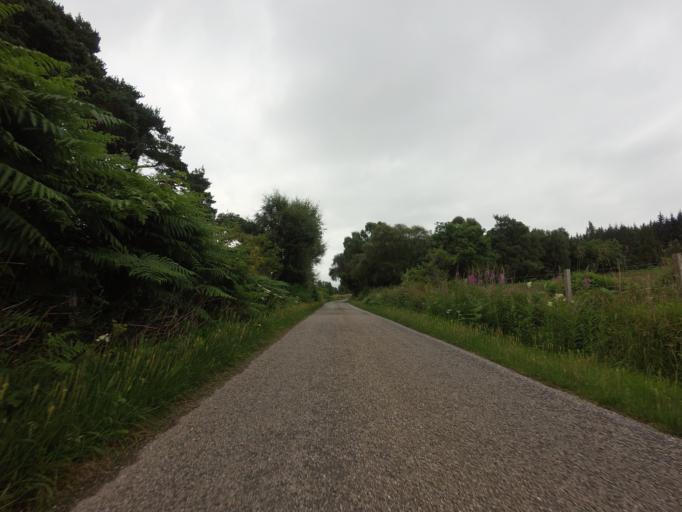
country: GB
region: Scotland
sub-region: Highland
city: Evanton
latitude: 57.9047
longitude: -4.3892
